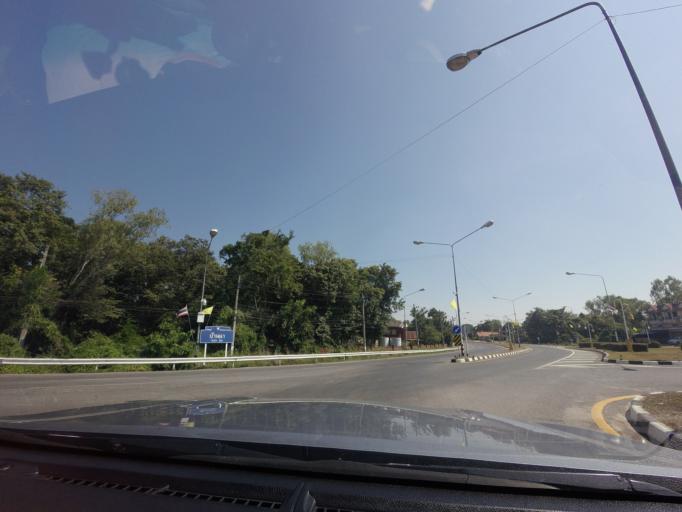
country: TH
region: Sukhothai
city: Ban Na
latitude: 17.0165
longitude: 99.7341
